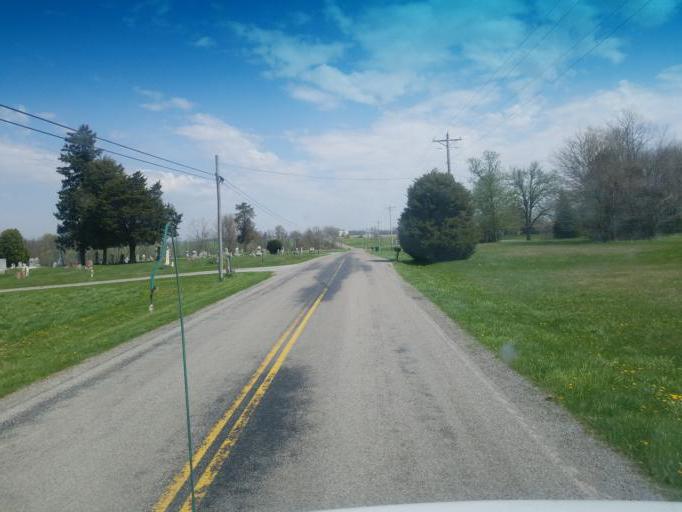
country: US
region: Ohio
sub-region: Hardin County
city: Kenton
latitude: 40.5974
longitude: -83.6723
